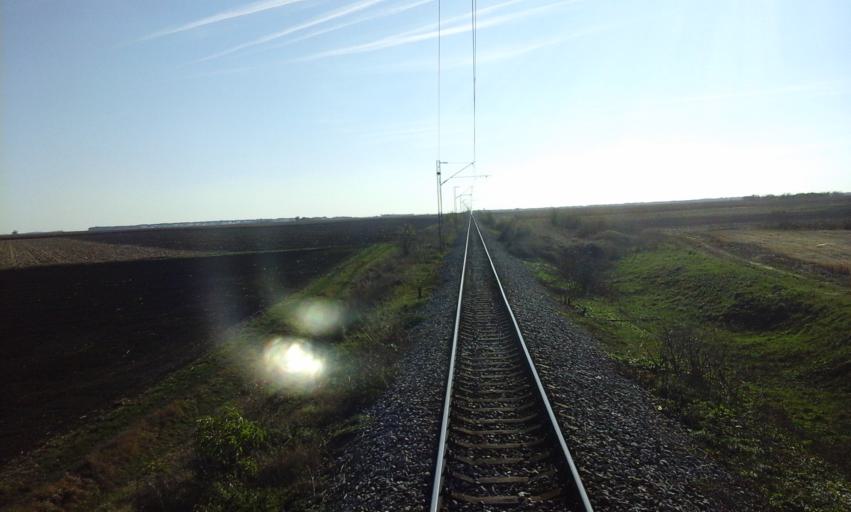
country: RS
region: Autonomna Pokrajina Vojvodina
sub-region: Severnobacki Okrug
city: Backa Topola
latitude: 45.9114
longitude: 19.6639
